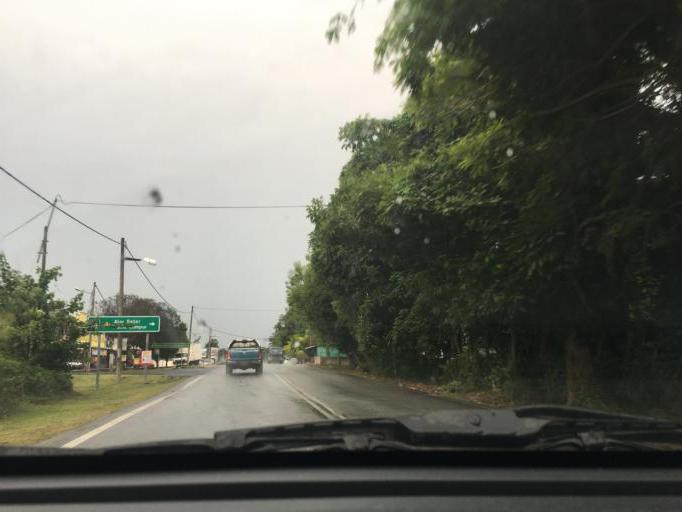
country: MY
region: Kedah
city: Sungai Petani
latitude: 5.6100
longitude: 100.6397
